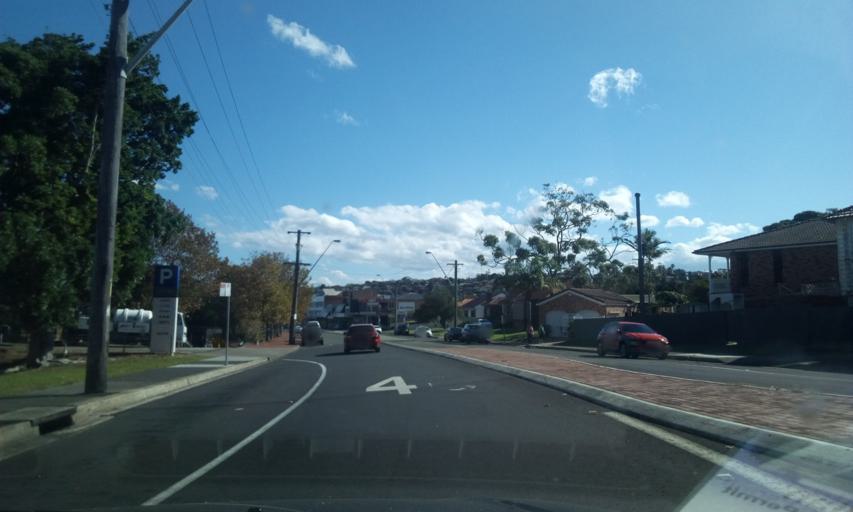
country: AU
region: New South Wales
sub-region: Wollongong
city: Port Kembla
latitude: -34.4854
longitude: 150.8913
